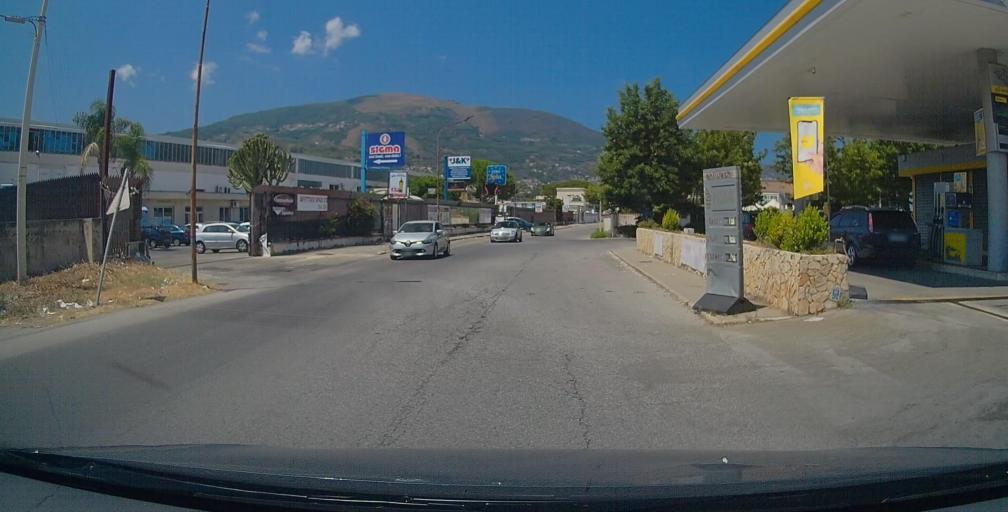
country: IT
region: Sicily
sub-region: Messina
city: Patti
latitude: 38.1487
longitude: 14.9804
